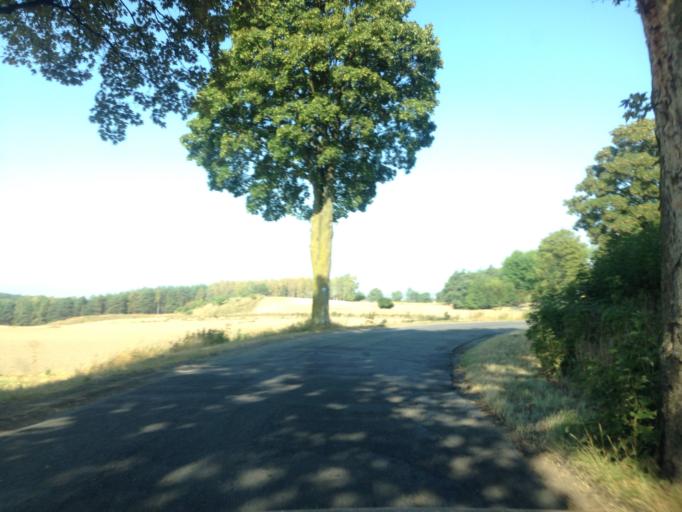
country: PL
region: Kujawsko-Pomorskie
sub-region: Powiat brodnicki
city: Brzozie
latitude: 53.2983
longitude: 19.6291
